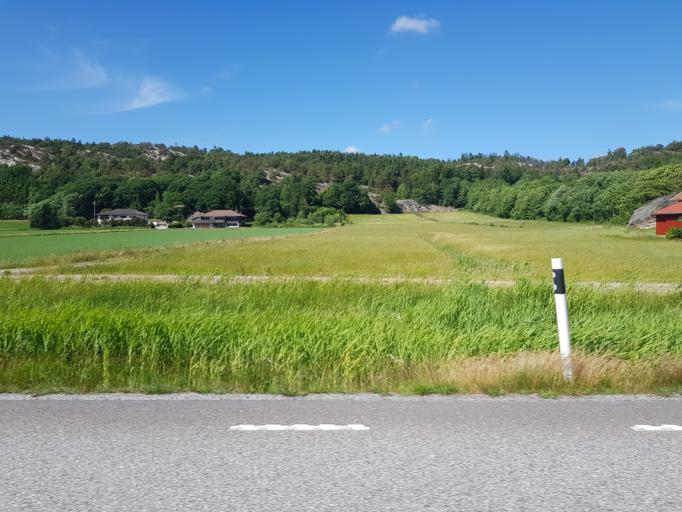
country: SE
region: Vaestra Goetaland
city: Ronnang
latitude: 57.9660
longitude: 11.6269
